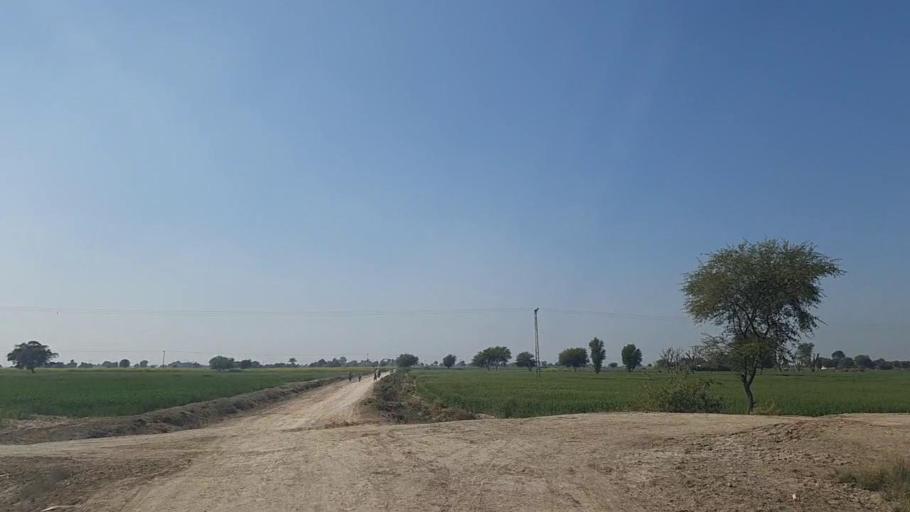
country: PK
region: Sindh
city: Shahpur Chakar
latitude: 26.2142
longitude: 68.5766
